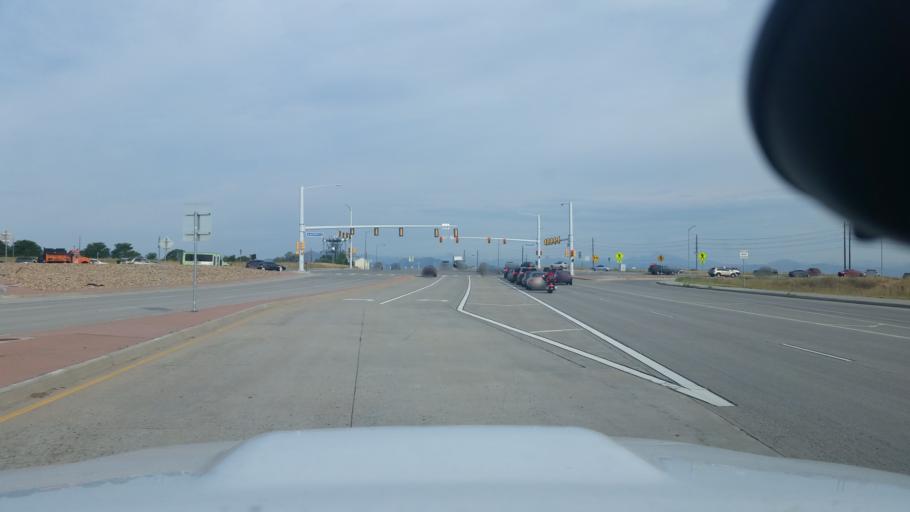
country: US
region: Colorado
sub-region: Broomfield County
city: Broomfield
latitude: 39.9129
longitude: -105.0954
